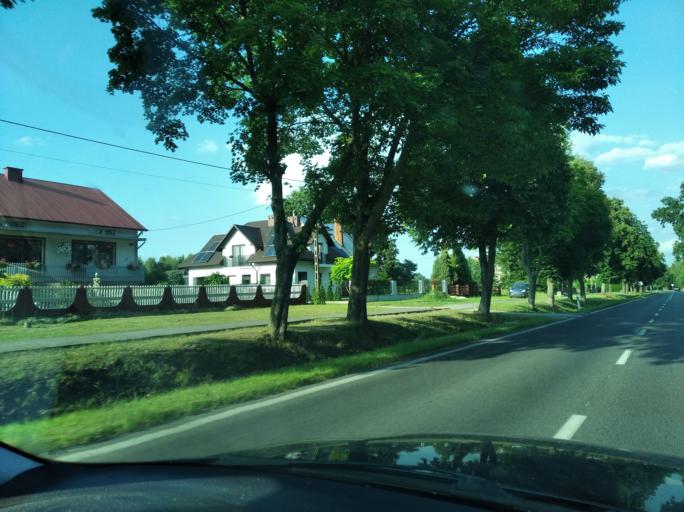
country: PL
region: Subcarpathian Voivodeship
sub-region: Powiat lezajski
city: Brzoza Krolewska
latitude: 50.2552
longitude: 22.2971
